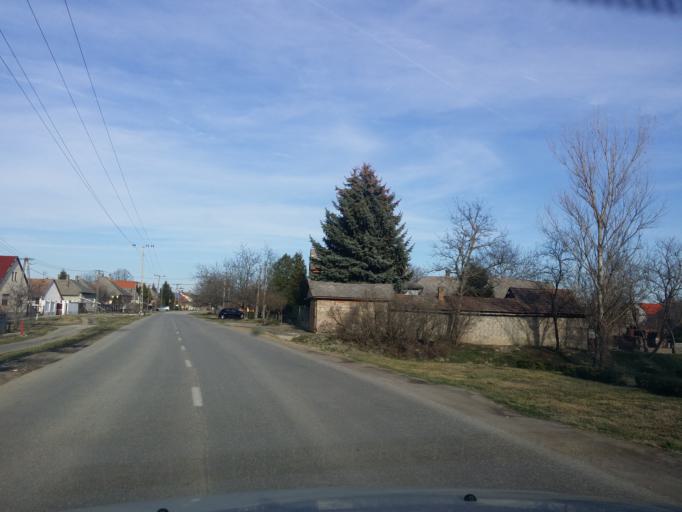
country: HU
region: Tolna
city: Madocsa
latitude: 46.6876
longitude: 18.9510
